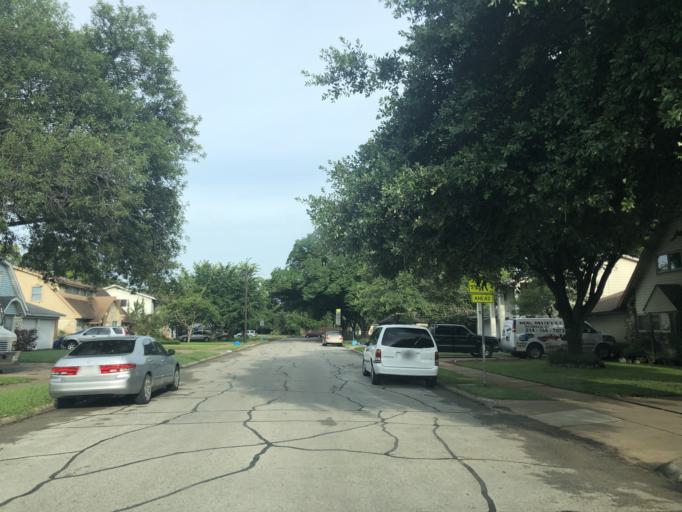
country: US
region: Texas
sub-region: Dallas County
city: Irving
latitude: 32.8048
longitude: -96.9751
